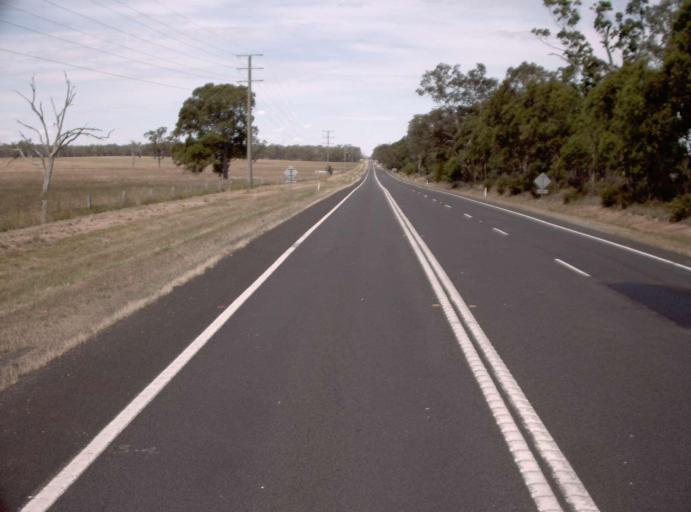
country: AU
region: Victoria
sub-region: Wellington
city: Sale
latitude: -37.9250
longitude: 147.2289
